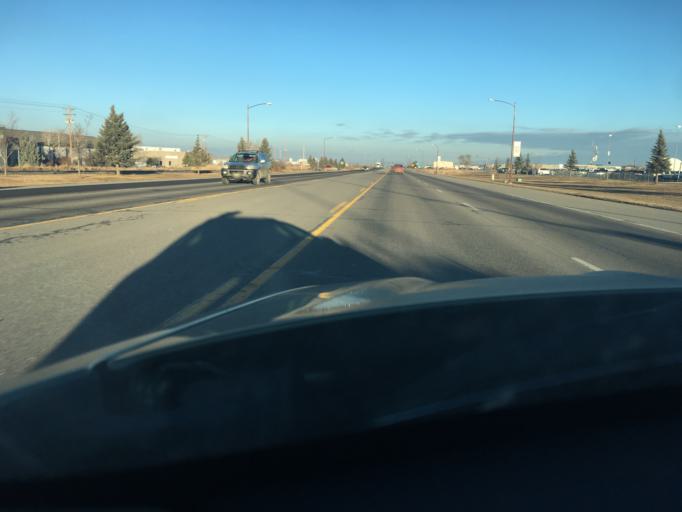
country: US
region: Colorado
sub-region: Montrose County
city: Montrose
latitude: 38.4990
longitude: -107.9000
